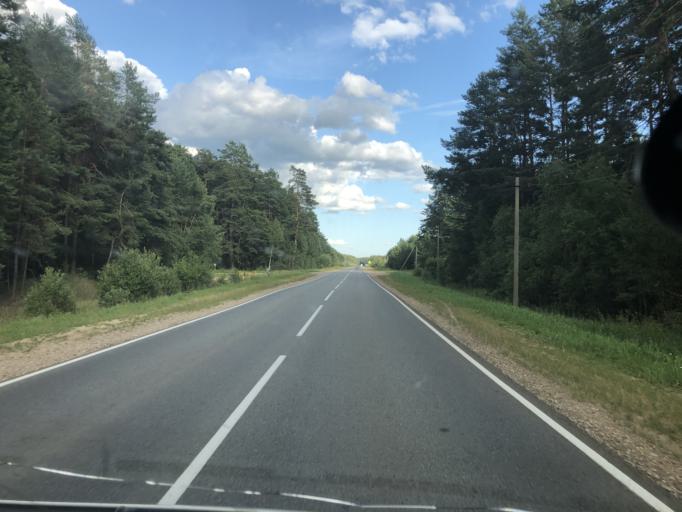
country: RU
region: Kaluga
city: Yukhnov
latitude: 54.7223
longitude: 35.2180
